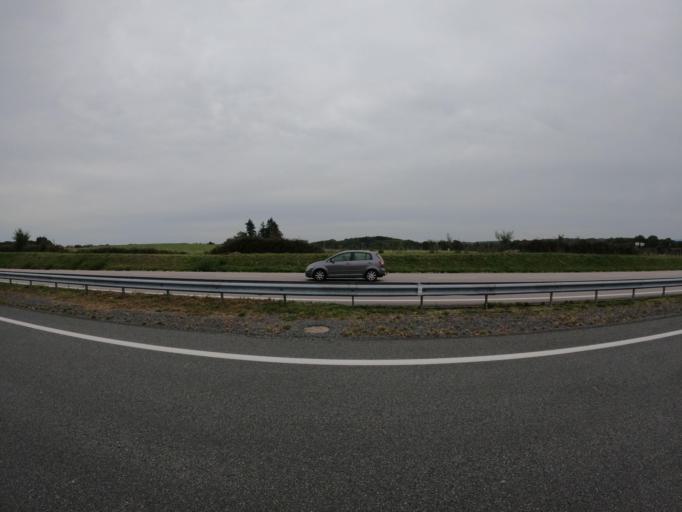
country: FR
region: Limousin
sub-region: Departement de la Creuse
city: La Souterraine
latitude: 46.2321
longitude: 1.5119
